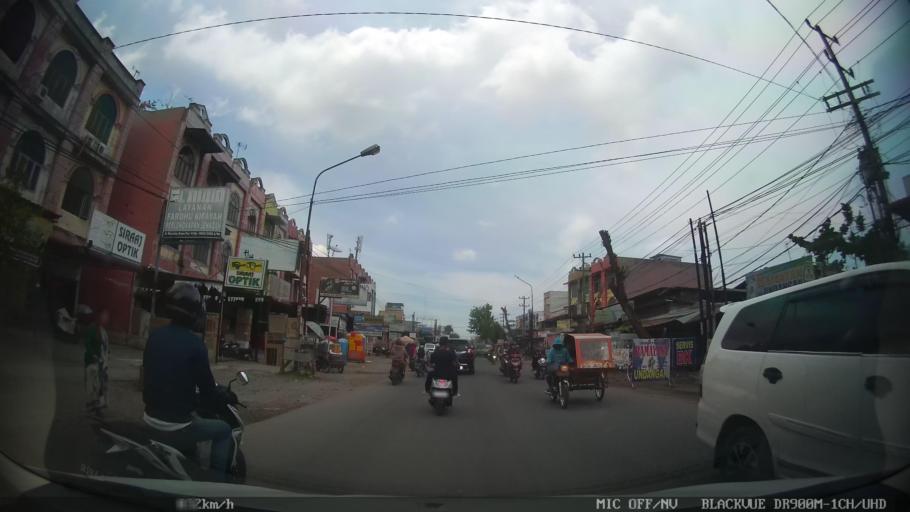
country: ID
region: North Sumatra
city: Labuhan Deli
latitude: 3.6952
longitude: 98.6559
